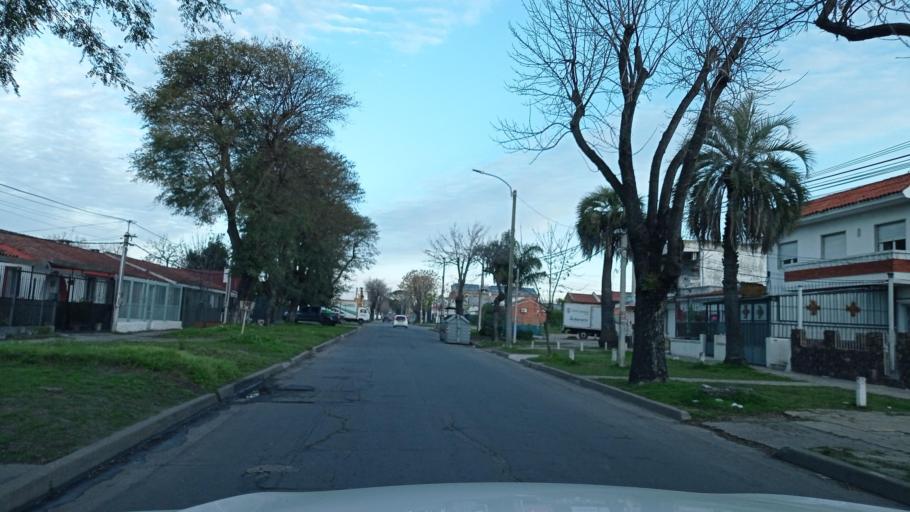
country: UY
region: Montevideo
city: Montevideo
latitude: -34.8657
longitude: -56.1484
